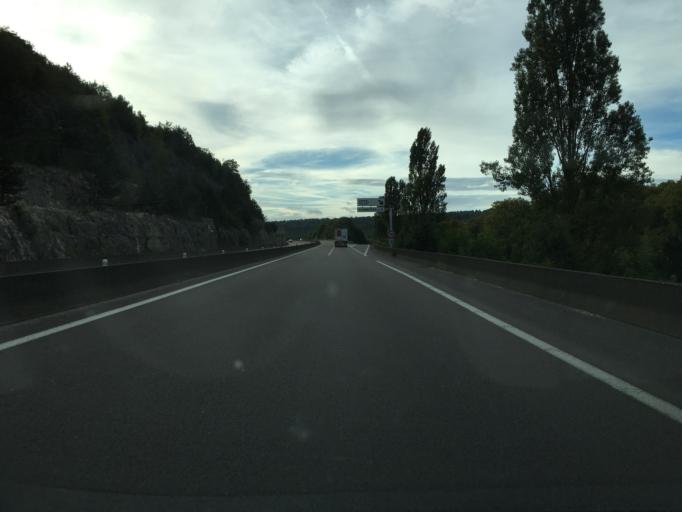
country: FR
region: Bourgogne
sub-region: Departement de la Cote-d'Or
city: Plombieres-les-Dijon
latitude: 47.3349
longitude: 4.9740
